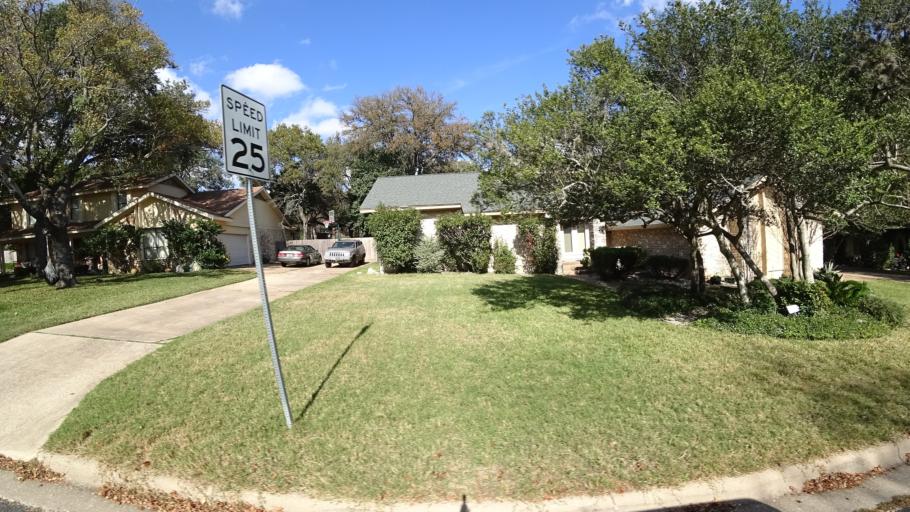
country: US
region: Texas
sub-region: Williamson County
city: Anderson Mill
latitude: 30.4303
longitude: -97.8048
